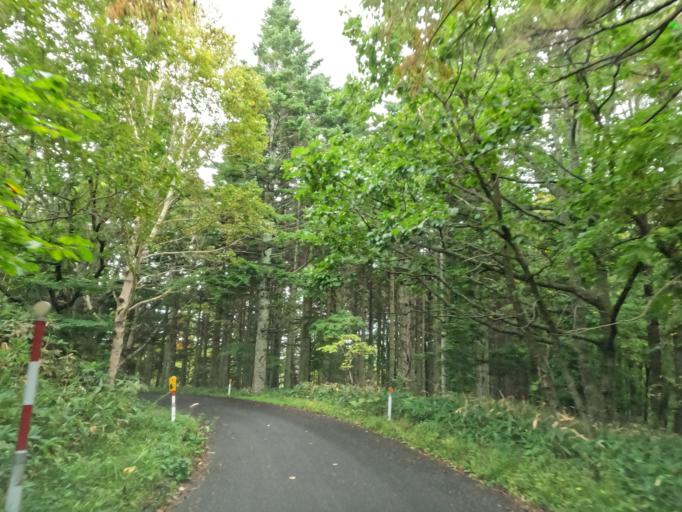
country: JP
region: Hokkaido
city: Date
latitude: 42.4789
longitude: 140.9060
